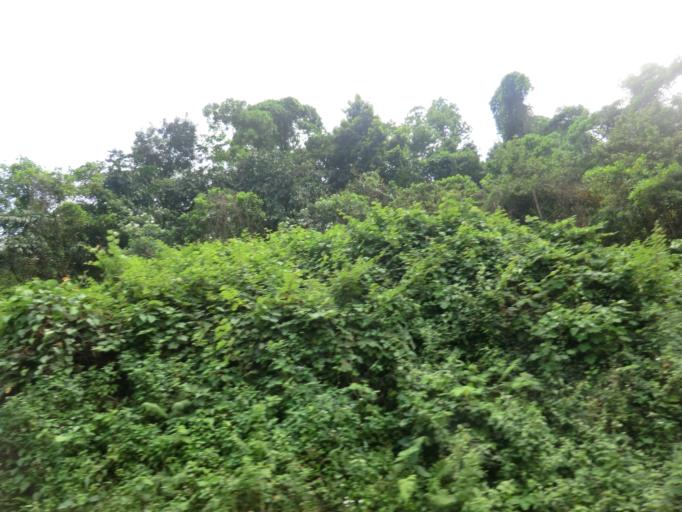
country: VN
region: Da Nang
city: Lien Chieu
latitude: 16.2203
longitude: 108.0990
